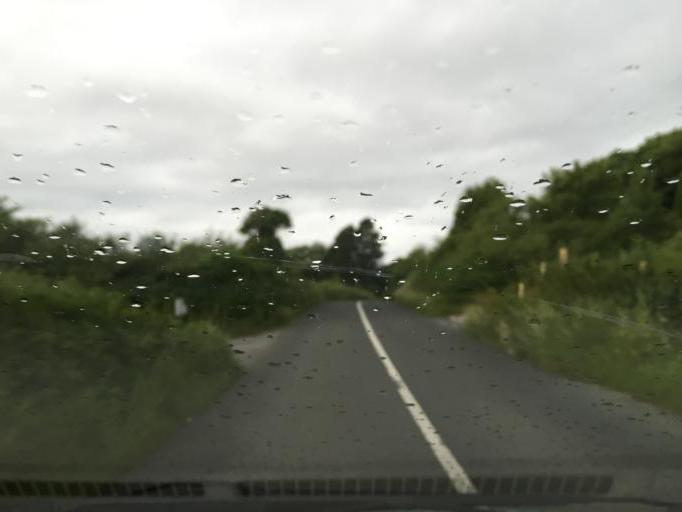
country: IE
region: Connaught
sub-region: Sligo
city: Strandhill
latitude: 54.2507
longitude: -8.5858
